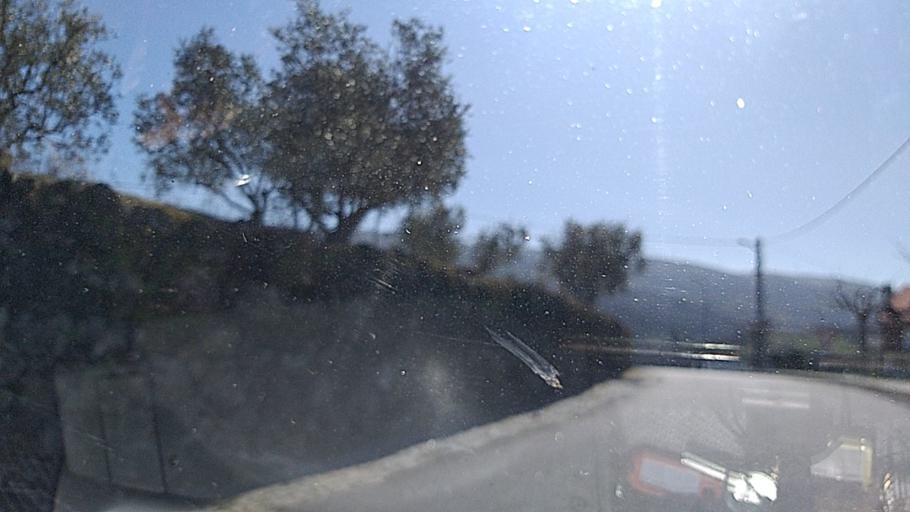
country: PT
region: Guarda
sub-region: Celorico da Beira
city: Celorico da Beira
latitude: 40.6173
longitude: -7.4072
